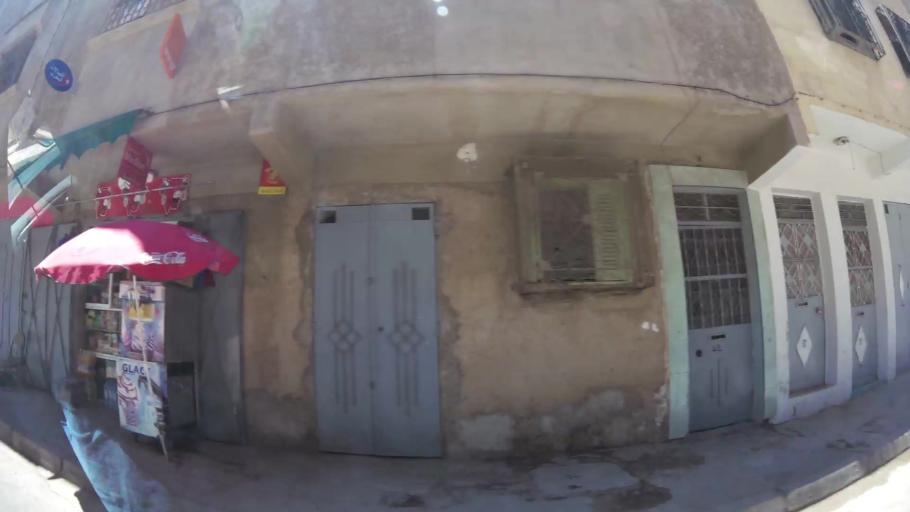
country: MA
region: Oriental
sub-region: Oujda-Angad
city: Oujda
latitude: 34.6600
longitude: -1.9231
